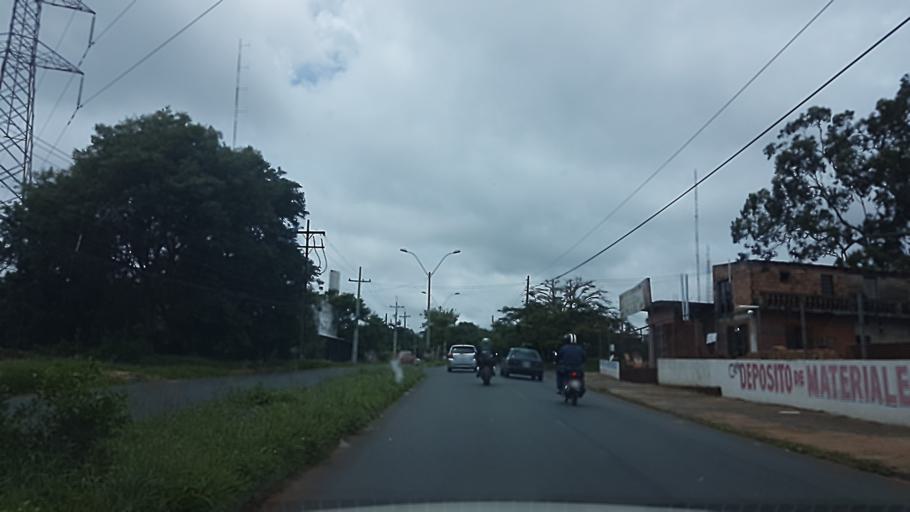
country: PY
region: Central
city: Villa Elisa
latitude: -25.3889
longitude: -57.5828
